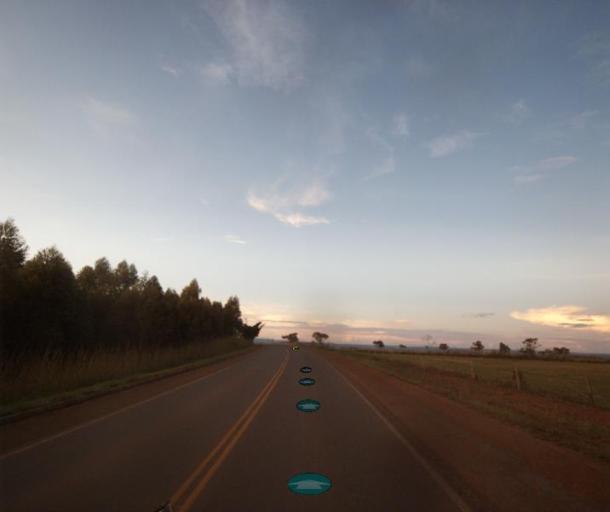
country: BR
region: Goias
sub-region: Pirenopolis
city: Pirenopolis
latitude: -16.0189
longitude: -48.8375
